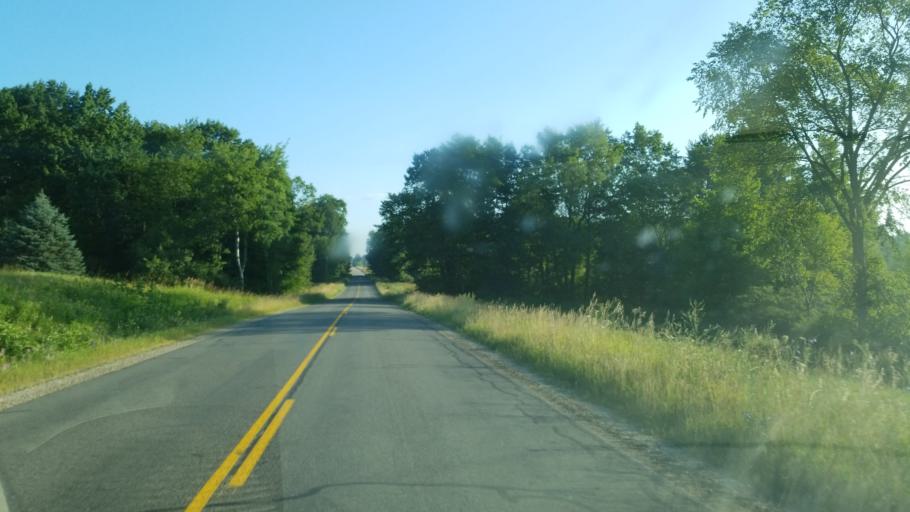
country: US
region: Michigan
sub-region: Mecosta County
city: Canadian Lakes
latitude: 43.5351
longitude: -85.1846
